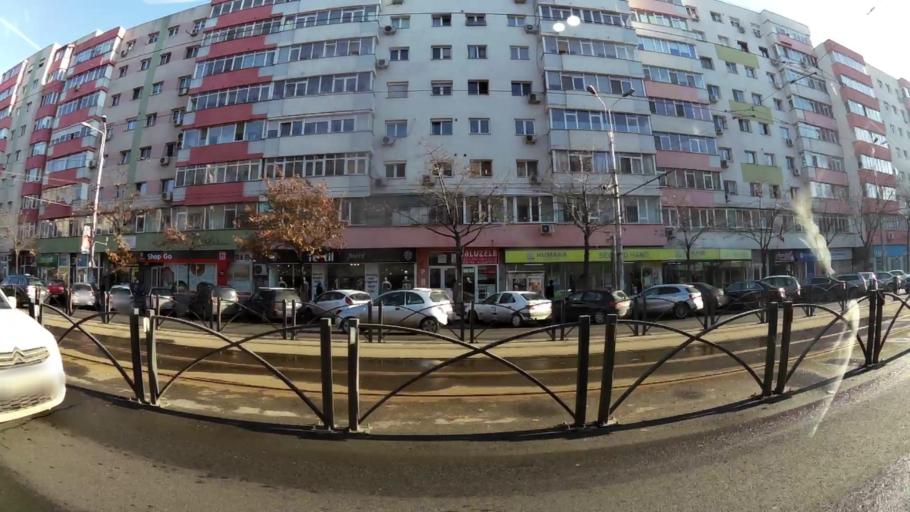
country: RO
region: Bucuresti
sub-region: Municipiul Bucuresti
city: Bucharest
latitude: 44.4398
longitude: 26.1166
